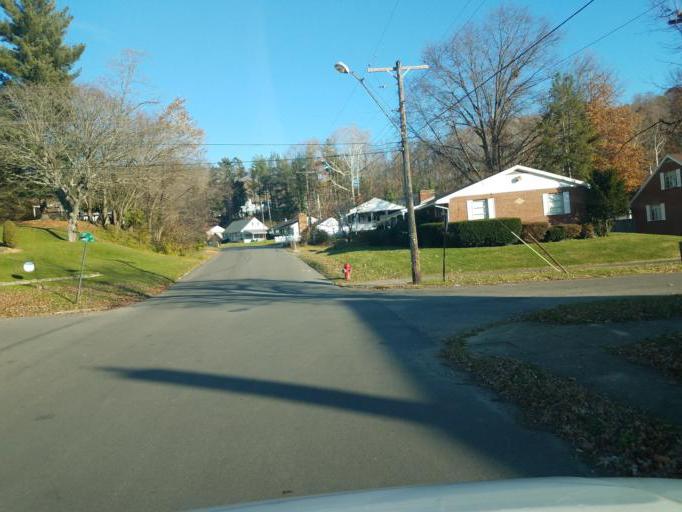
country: US
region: Ohio
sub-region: Scioto County
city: Portsmouth
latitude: 38.7497
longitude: -82.9739
